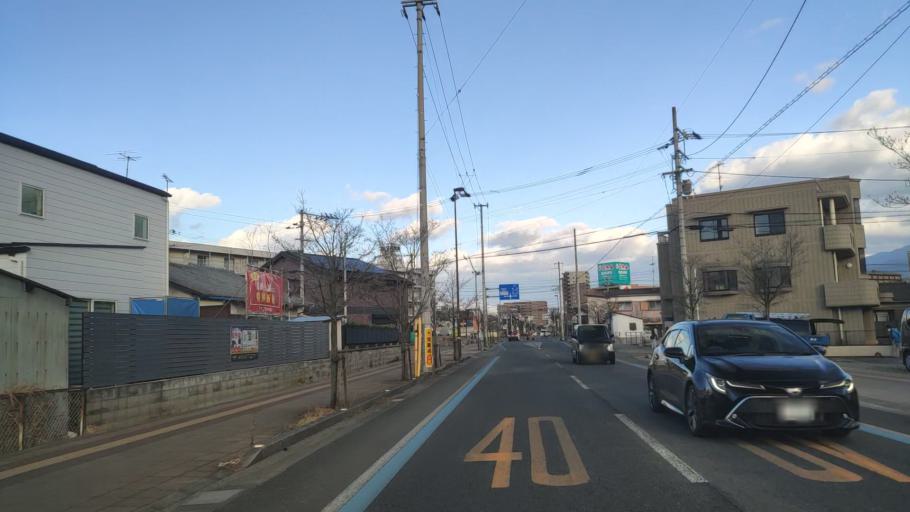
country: JP
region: Ehime
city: Saijo
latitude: 33.9163
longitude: 133.1761
